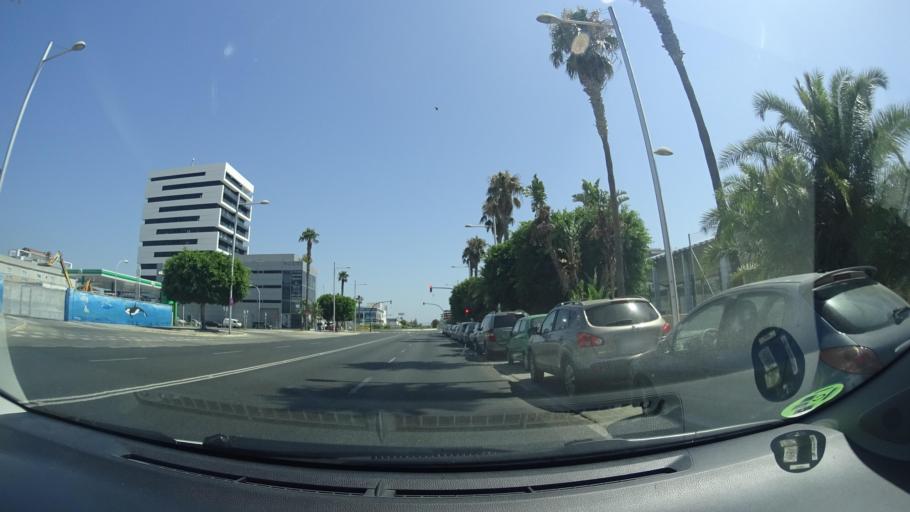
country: ES
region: Andalusia
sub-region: Provincia de Cadiz
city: Cadiz
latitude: 36.5017
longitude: -6.2715
